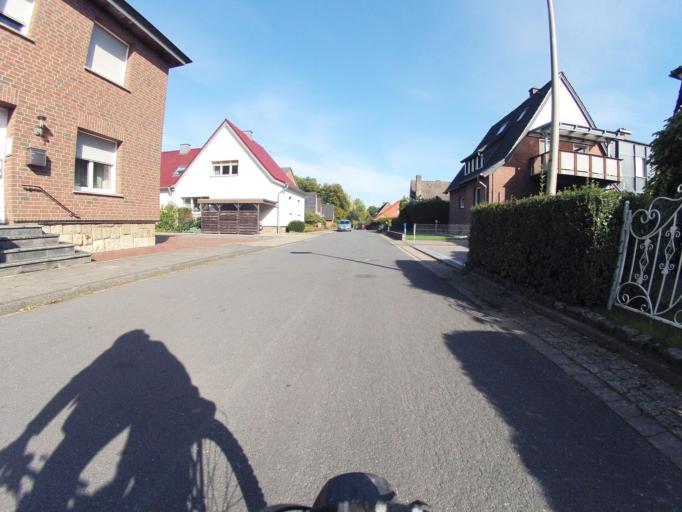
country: DE
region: North Rhine-Westphalia
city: Ibbenburen
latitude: 52.2647
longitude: 7.7108
